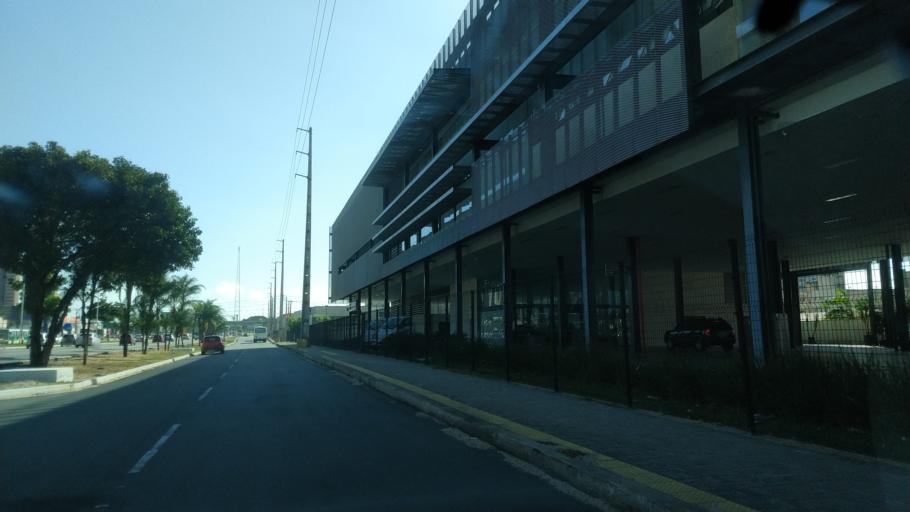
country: BR
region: Rio Grande do Norte
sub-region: Natal
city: Natal
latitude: -5.8537
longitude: -35.2107
